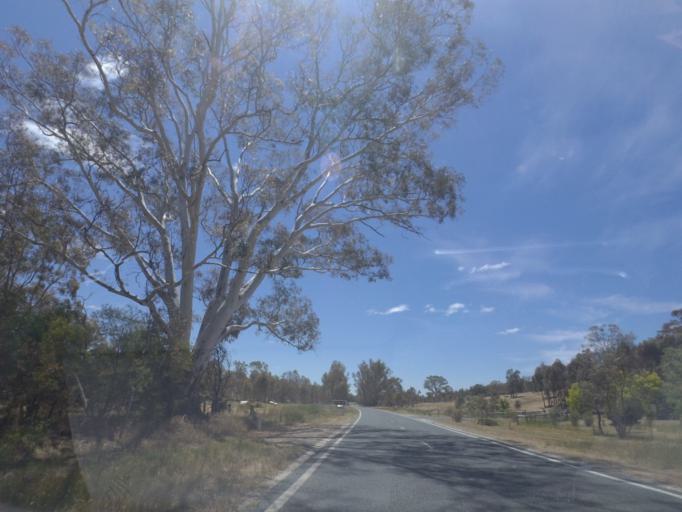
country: AU
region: Victoria
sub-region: Mount Alexander
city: Castlemaine
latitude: -37.1783
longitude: 144.1475
